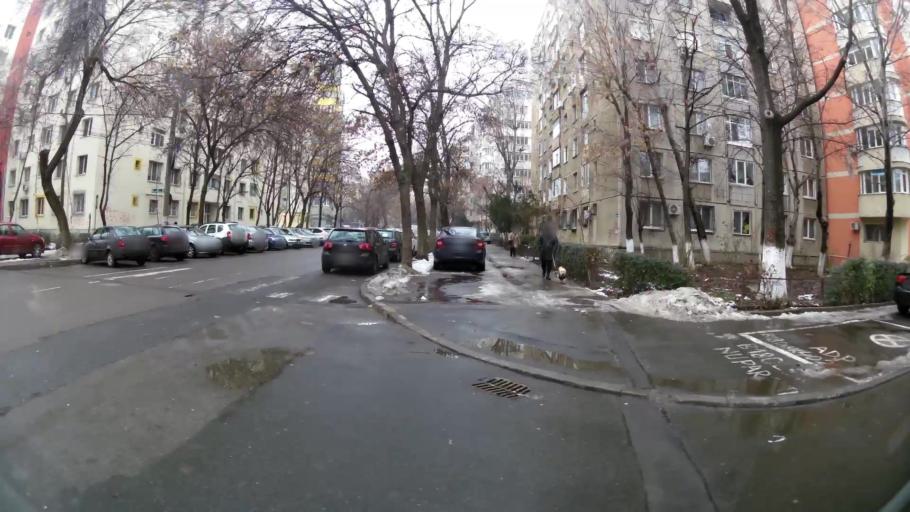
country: RO
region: Bucuresti
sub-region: Municipiul Bucuresti
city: Bucharest
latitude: 44.4601
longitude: 26.1254
